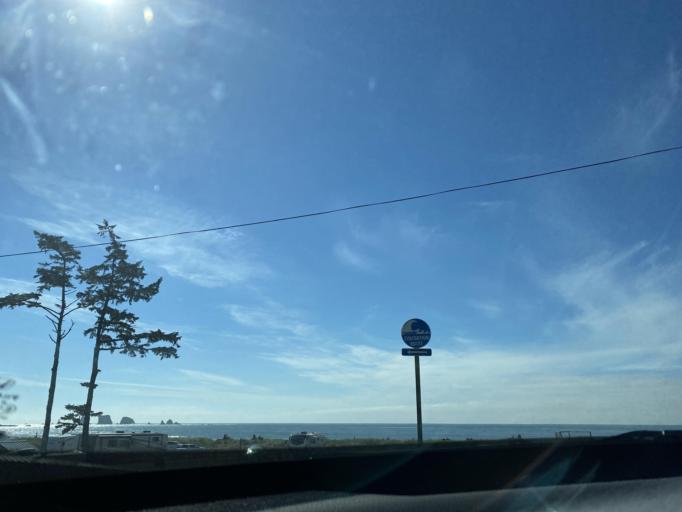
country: US
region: Washington
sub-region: Clallam County
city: Forks
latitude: 47.9079
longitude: -124.6355
